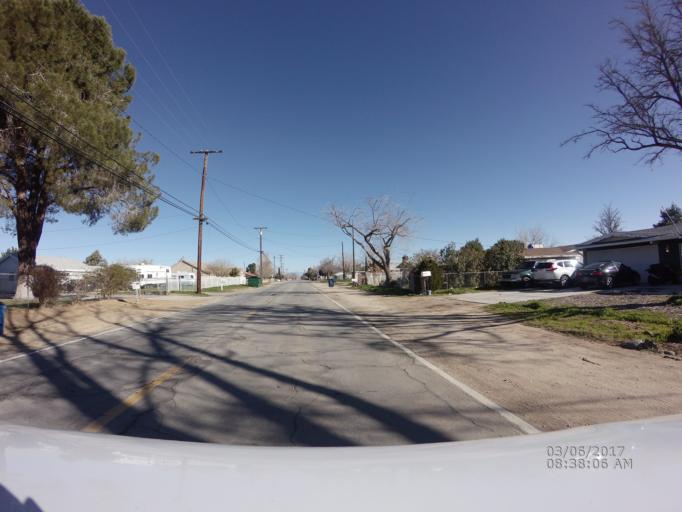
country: US
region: California
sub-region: Los Angeles County
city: Quartz Hill
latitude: 34.6643
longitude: -118.2101
